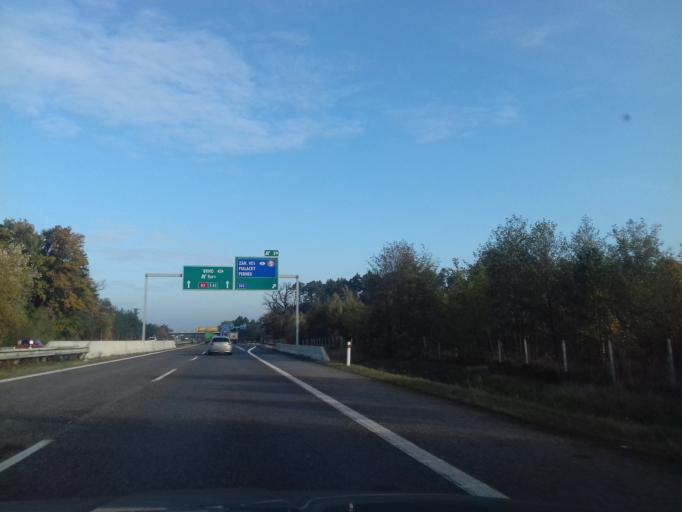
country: SK
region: Bratislavsky
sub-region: Okres Malacky
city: Malacky
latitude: 48.4235
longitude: 17.0413
